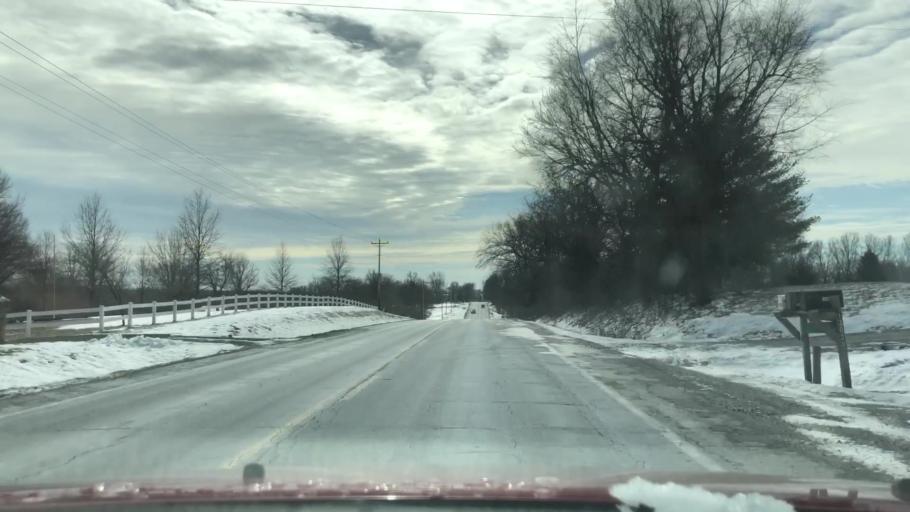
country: US
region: Missouri
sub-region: Jackson County
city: Lone Jack
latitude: 38.8779
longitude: -94.1352
